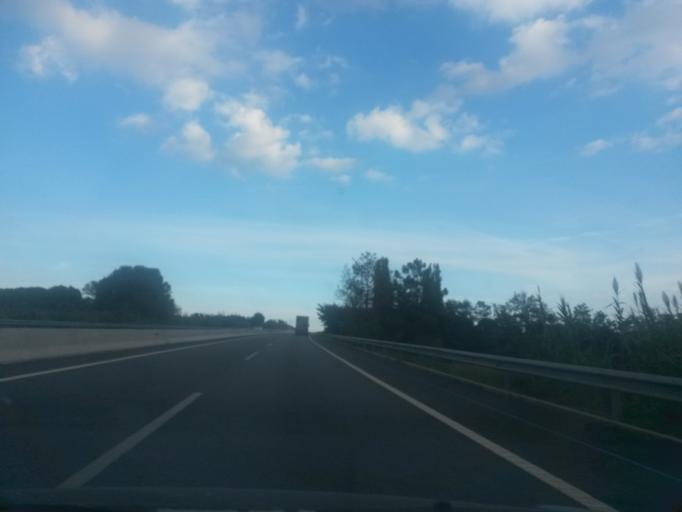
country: ES
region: Catalonia
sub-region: Provincia de Girona
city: Vilobi d'Onyar
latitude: 41.8794
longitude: 2.7319
